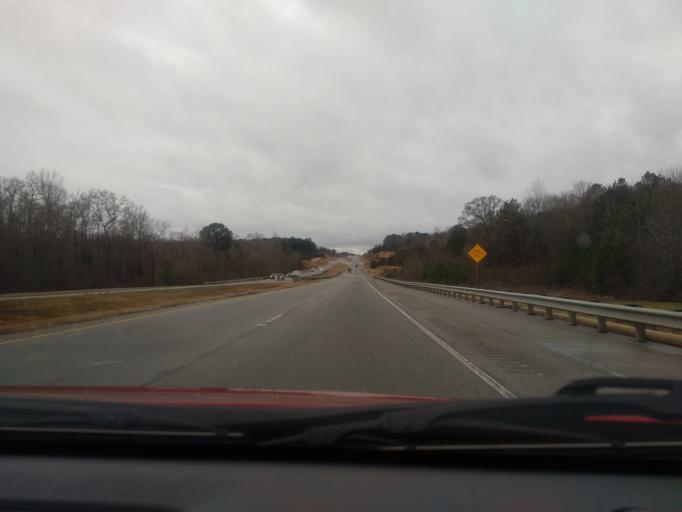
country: US
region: Georgia
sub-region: Spalding County
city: East Griffin
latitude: 33.2524
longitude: -84.1449
